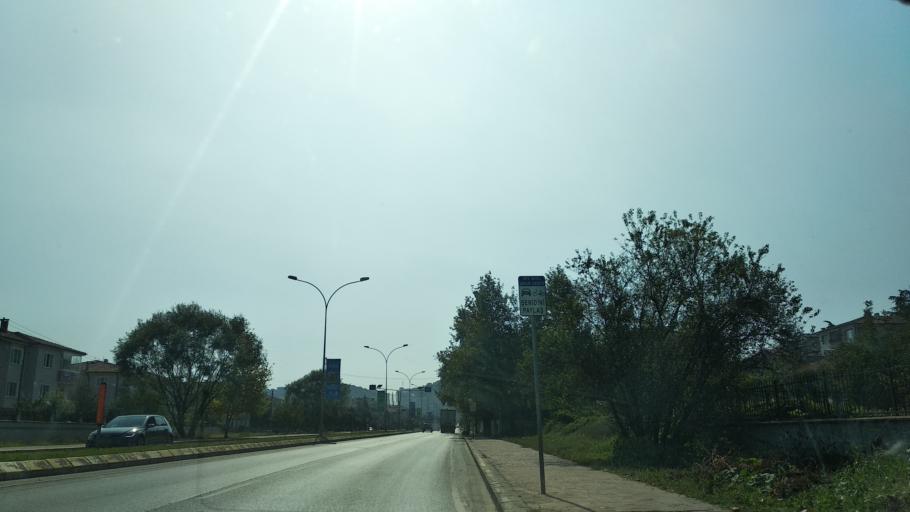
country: TR
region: Sakarya
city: Adapazari
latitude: 40.7674
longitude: 30.3638
